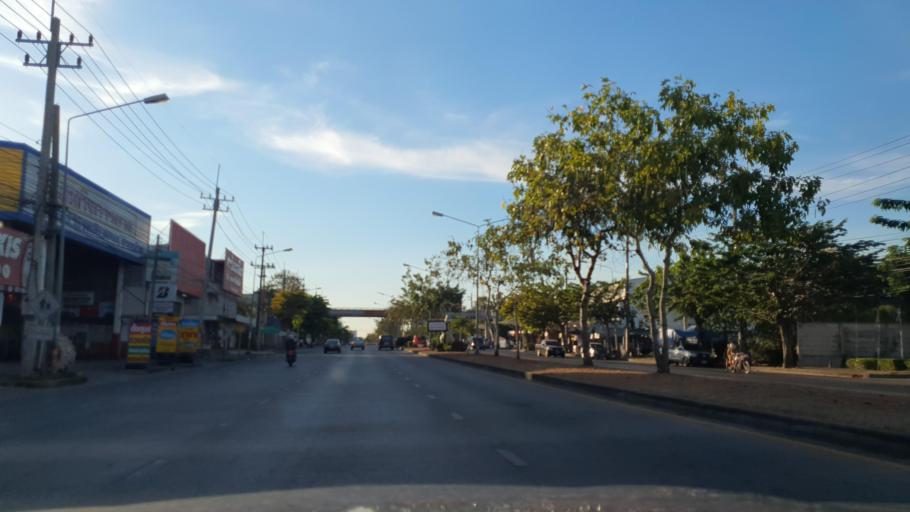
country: TH
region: Khon Kaen
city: Khon Kaen
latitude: 16.4268
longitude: 102.8743
